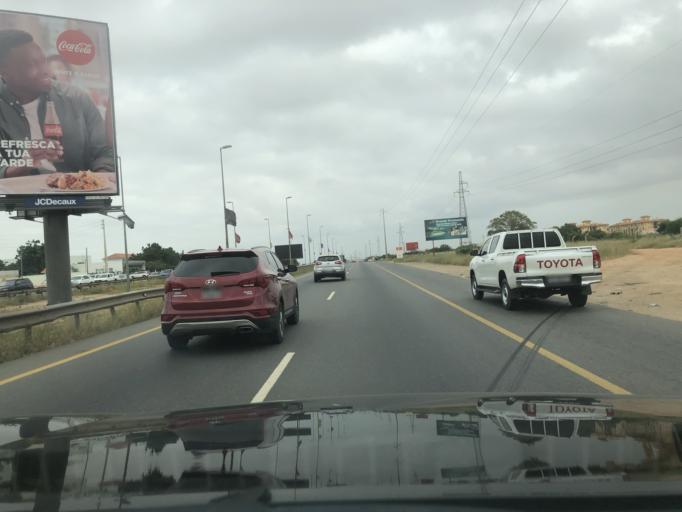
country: AO
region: Luanda
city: Luanda
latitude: -8.9733
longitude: 13.2400
